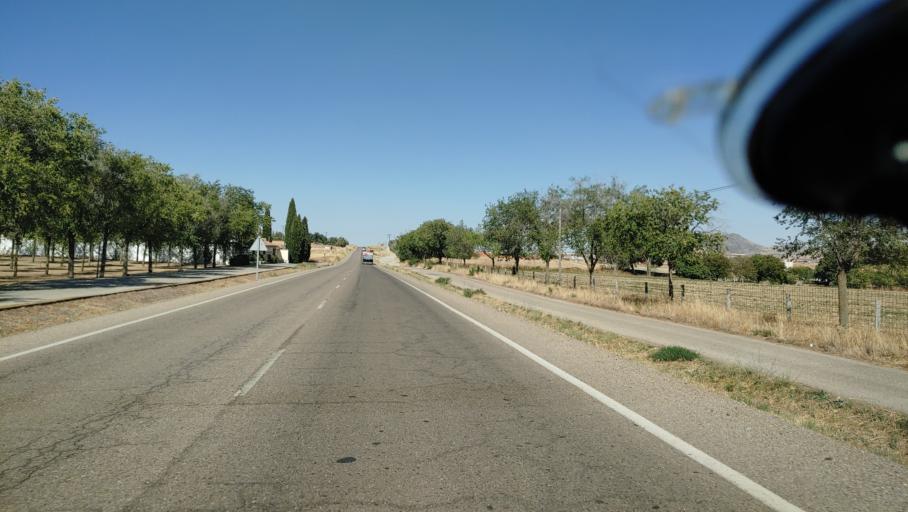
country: ES
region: Castille-La Mancha
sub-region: Province of Toledo
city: Pulgar
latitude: 39.7003
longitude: -4.1459
